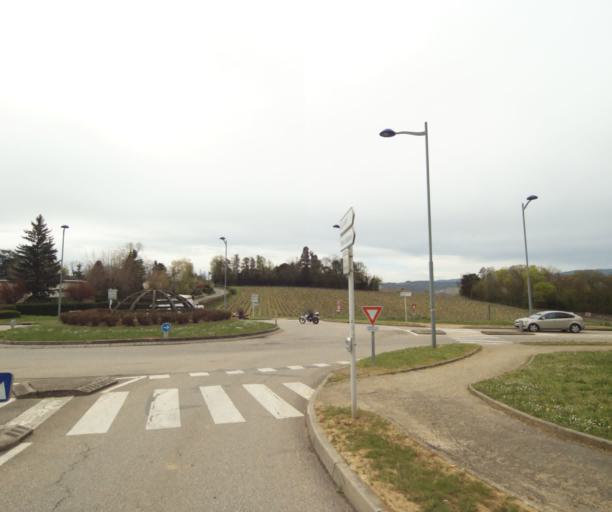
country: FR
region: Bourgogne
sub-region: Departement de Saone-et-Loire
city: Charnay-les-Macon
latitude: 46.3131
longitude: 4.7858
